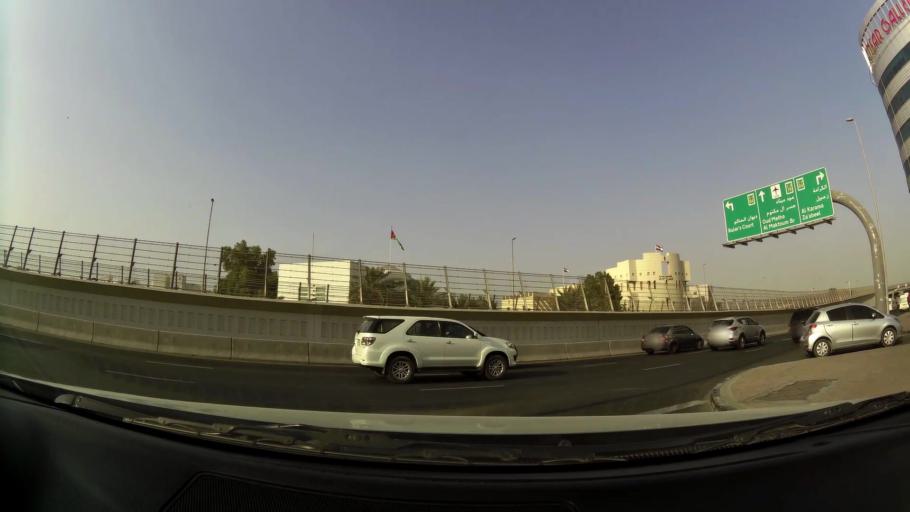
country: AE
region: Ash Shariqah
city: Sharjah
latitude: 25.2528
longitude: 55.3080
